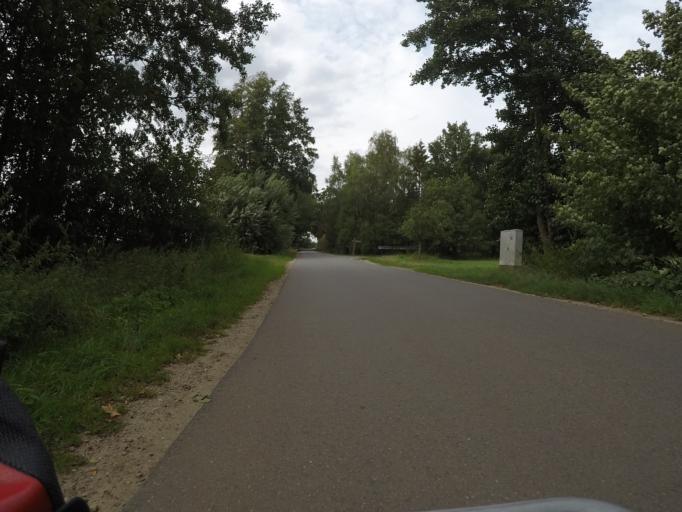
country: DE
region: Lower Saxony
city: Bardowick
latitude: 53.3053
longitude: 10.4039
